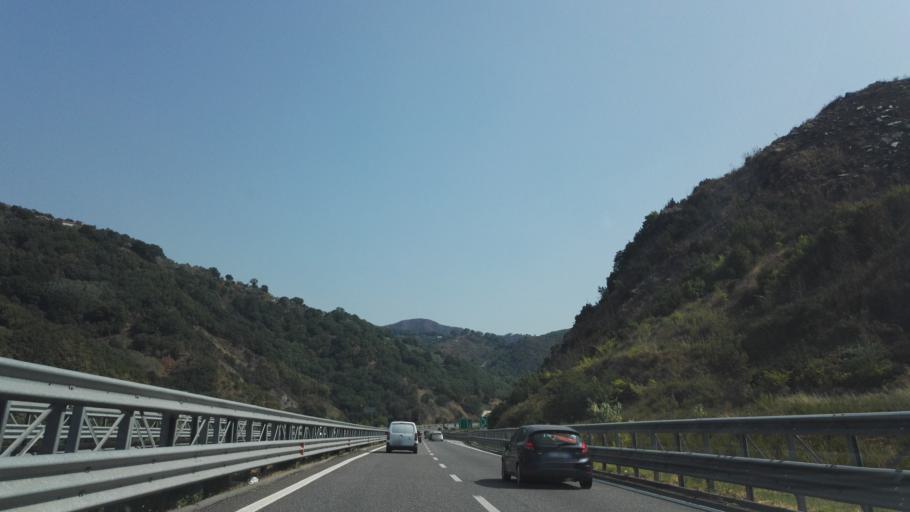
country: IT
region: Calabria
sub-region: Provincia di Catanzaro
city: San Mango d'Aquino
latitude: 39.0756
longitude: 16.1912
